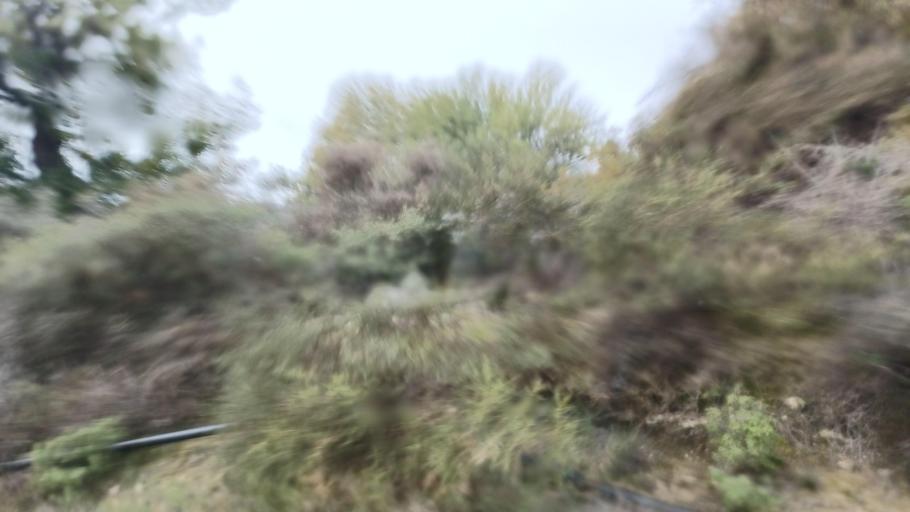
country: CY
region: Limassol
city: Pachna
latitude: 34.7471
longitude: 32.7338
